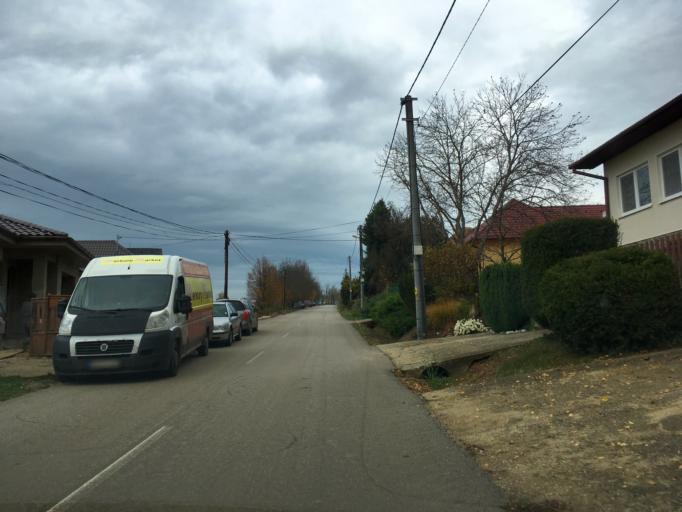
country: SK
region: Nitriansky
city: Svodin
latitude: 48.0205
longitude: 18.4077
